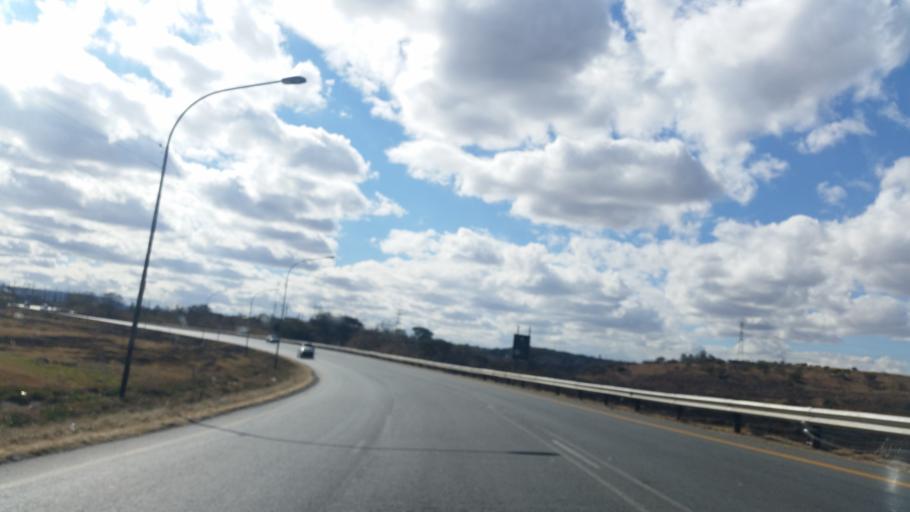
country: ZA
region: KwaZulu-Natal
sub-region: uThukela District Municipality
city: Ladysmith
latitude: -28.5483
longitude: 29.7940
